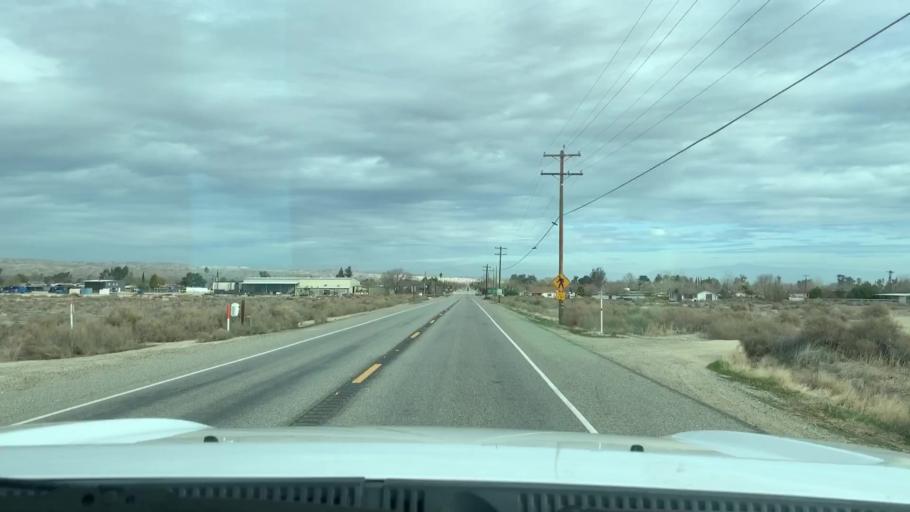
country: US
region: California
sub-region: Kern County
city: Ford City
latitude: 35.2037
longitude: -119.4140
